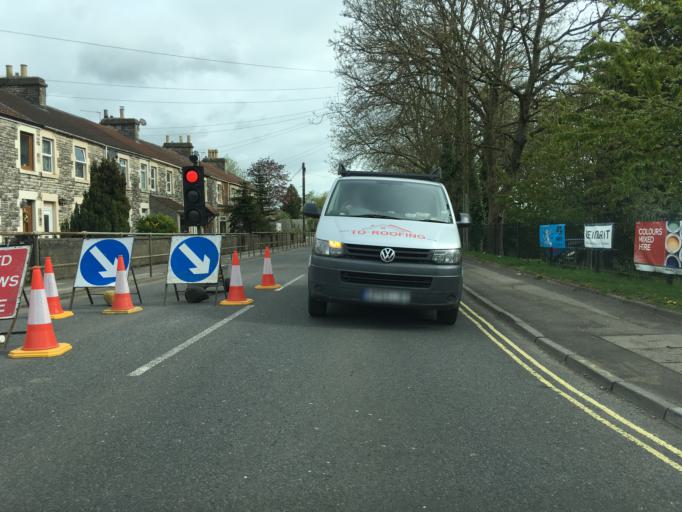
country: GB
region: England
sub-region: Bath and North East Somerset
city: Radstock
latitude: 51.2801
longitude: -2.4720
